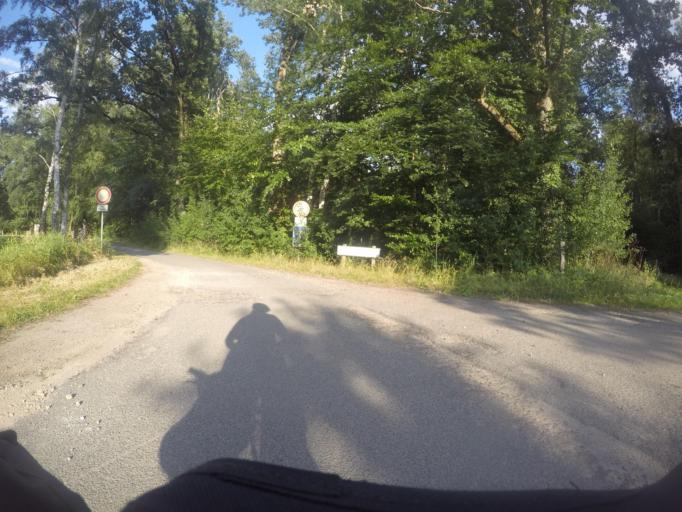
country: DE
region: Lower Saxony
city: Dahlenburg
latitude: 53.2039
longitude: 10.7188
